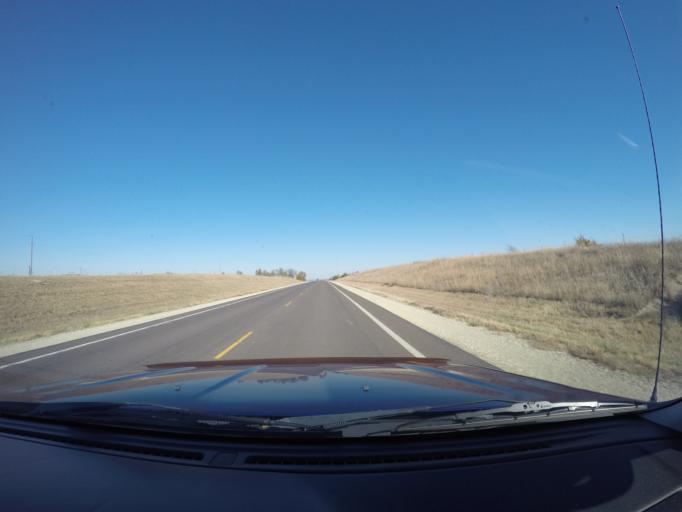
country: US
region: Kansas
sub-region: Marshall County
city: Blue Rapids
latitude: 39.6688
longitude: -96.7506
